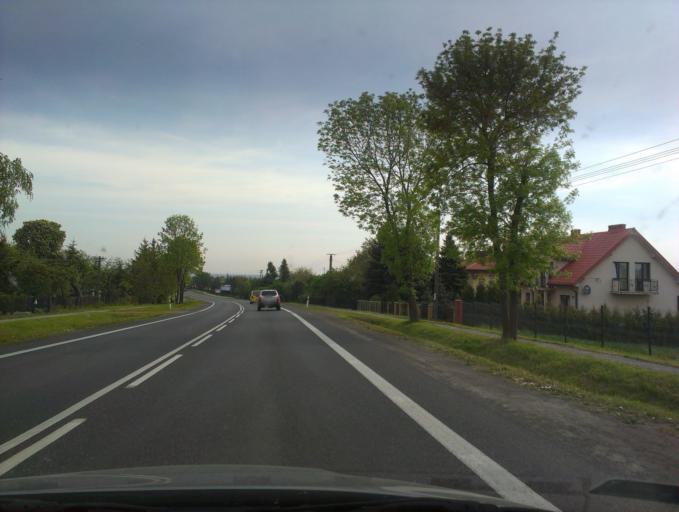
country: PL
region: Swietokrzyskie
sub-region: Powiat opatowski
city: Sadowie
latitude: 50.8896
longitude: 21.3760
